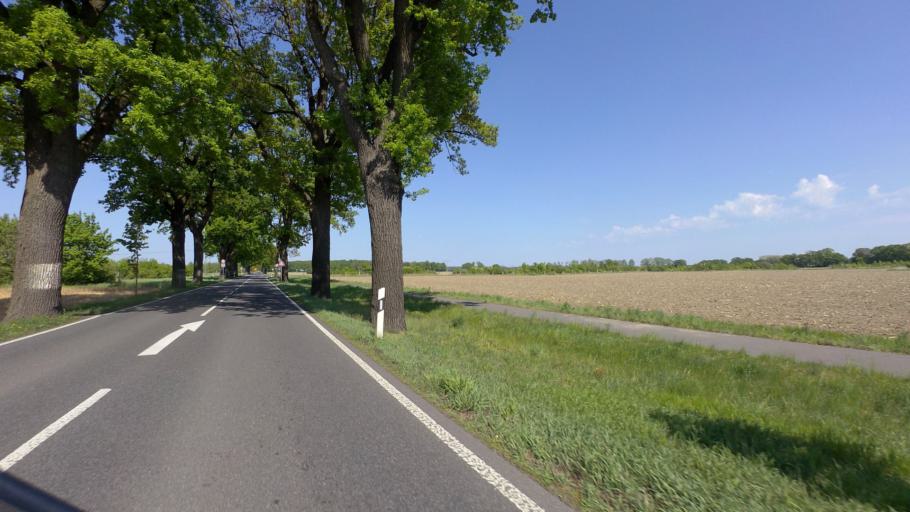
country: DE
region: Brandenburg
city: Beeskow
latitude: 52.1852
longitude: 14.2853
